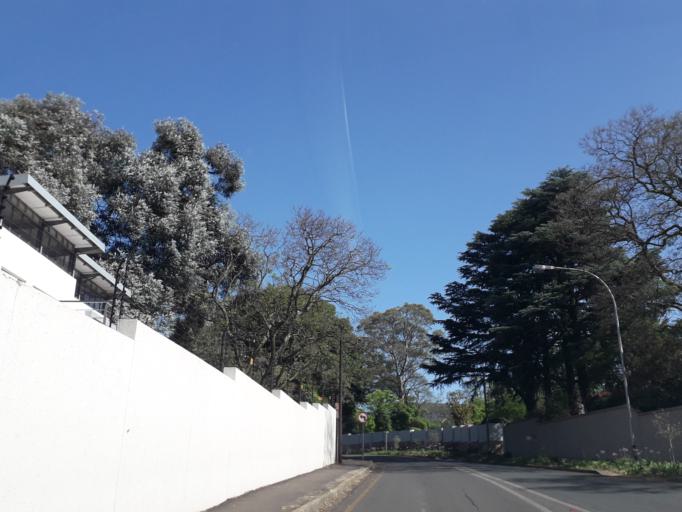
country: ZA
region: Gauteng
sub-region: City of Johannesburg Metropolitan Municipality
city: Johannesburg
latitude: -26.1738
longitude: 28.0603
